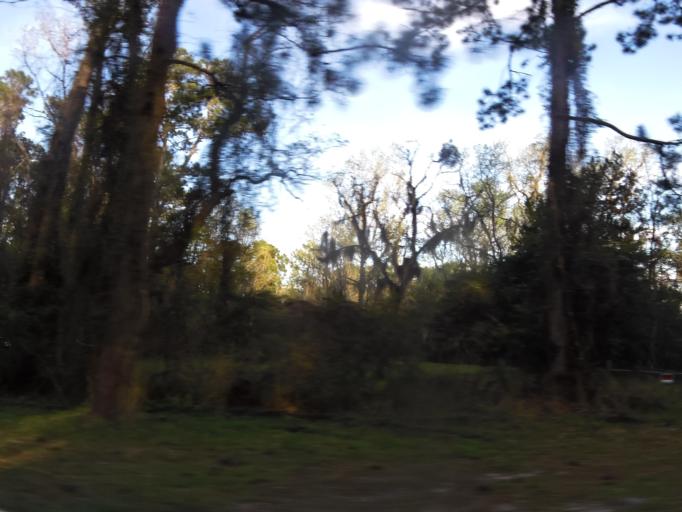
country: US
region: Florida
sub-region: Duval County
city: Jacksonville
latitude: 30.4343
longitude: -81.6716
